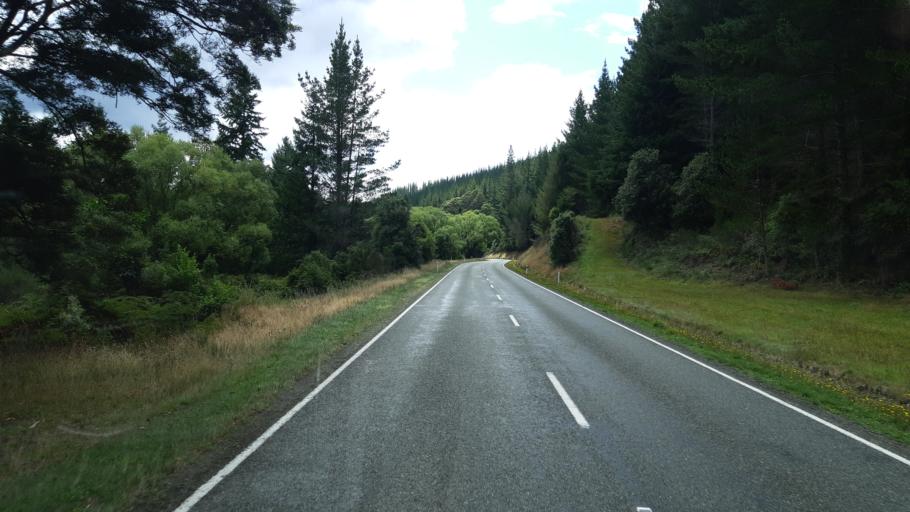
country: NZ
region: Tasman
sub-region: Tasman District
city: Wakefield
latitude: -41.5987
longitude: 172.7609
